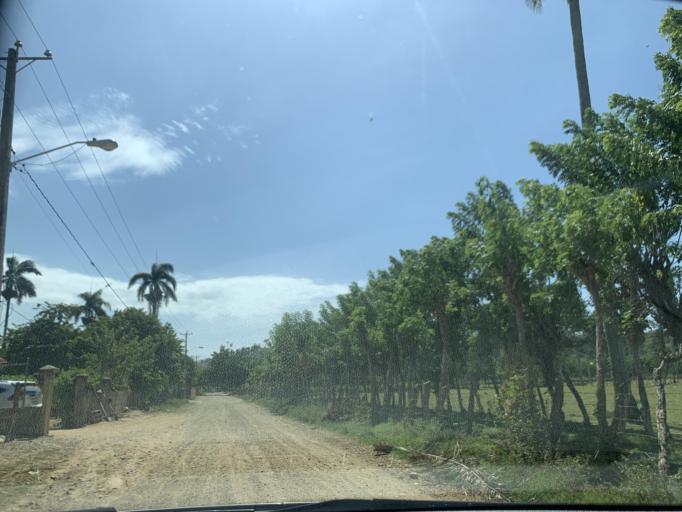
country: DO
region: Puerto Plata
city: Luperon
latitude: 19.8901
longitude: -70.8820
